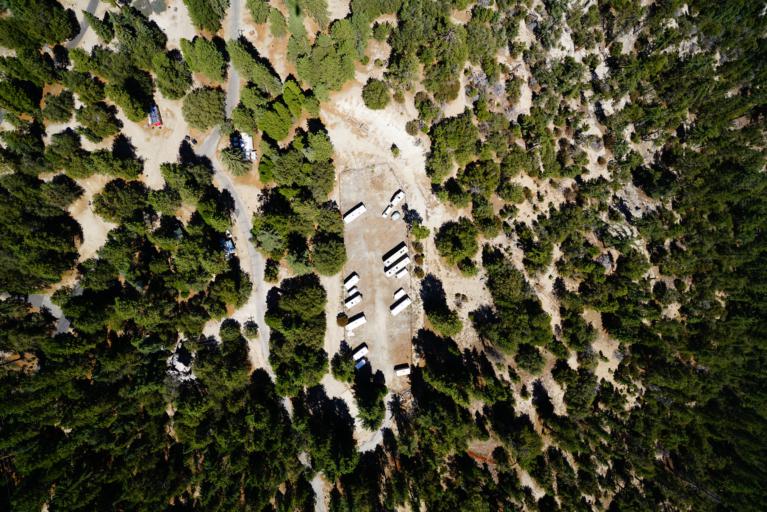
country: US
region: California
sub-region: Riverside County
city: Idyllwild-Pine Cove
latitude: 33.7698
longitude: -116.7260
